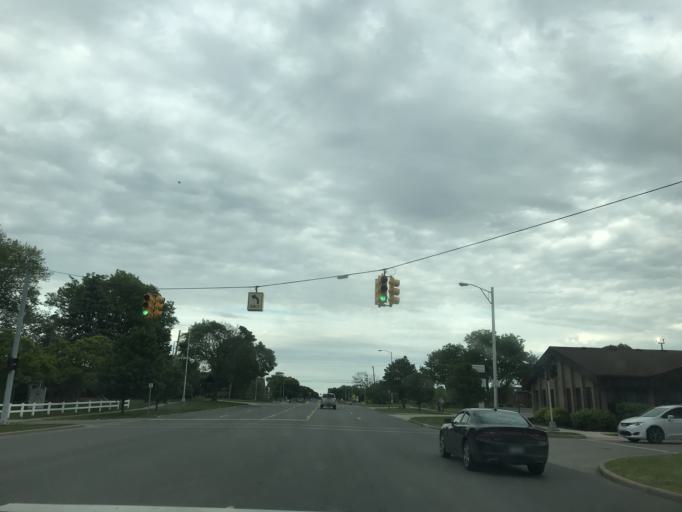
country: US
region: Michigan
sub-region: Wayne County
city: Trenton
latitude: 42.1410
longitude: -83.2089
